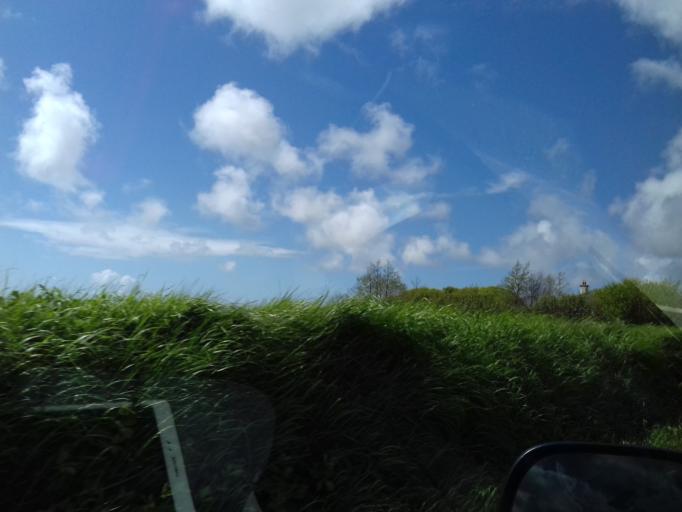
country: IE
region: Leinster
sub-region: Loch Garman
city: Loch Garman
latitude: 52.2818
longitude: -6.7002
